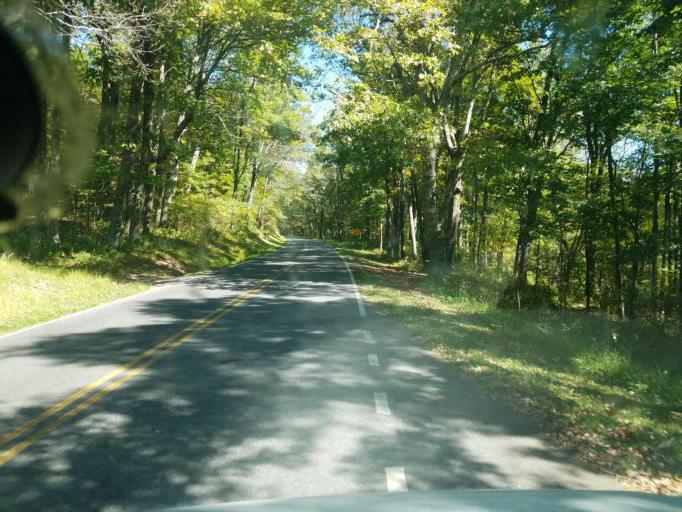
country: US
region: Virginia
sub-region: Rockingham County
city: Elkton
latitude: 38.3842
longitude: -78.5173
